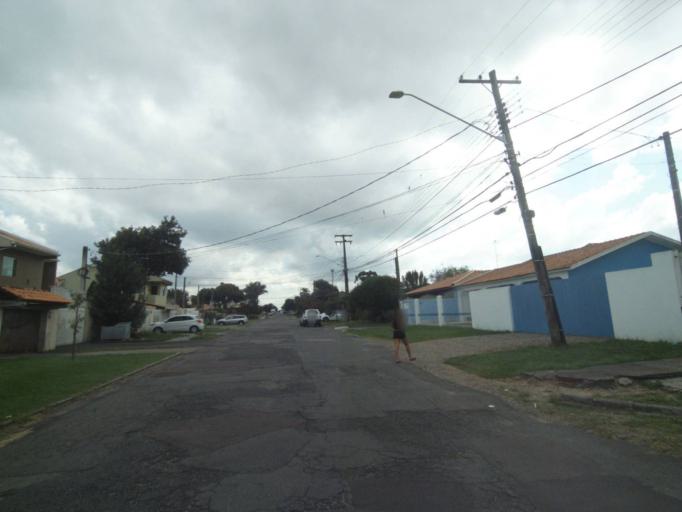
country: BR
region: Parana
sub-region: Pinhais
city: Pinhais
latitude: -25.4534
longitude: -49.2059
